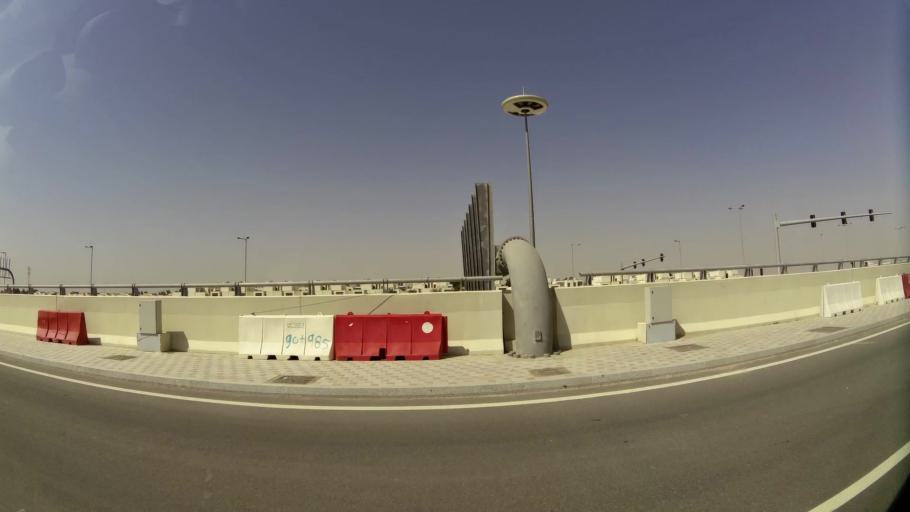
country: QA
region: Baladiyat ad Dawhah
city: Doha
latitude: 25.3885
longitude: 51.5190
